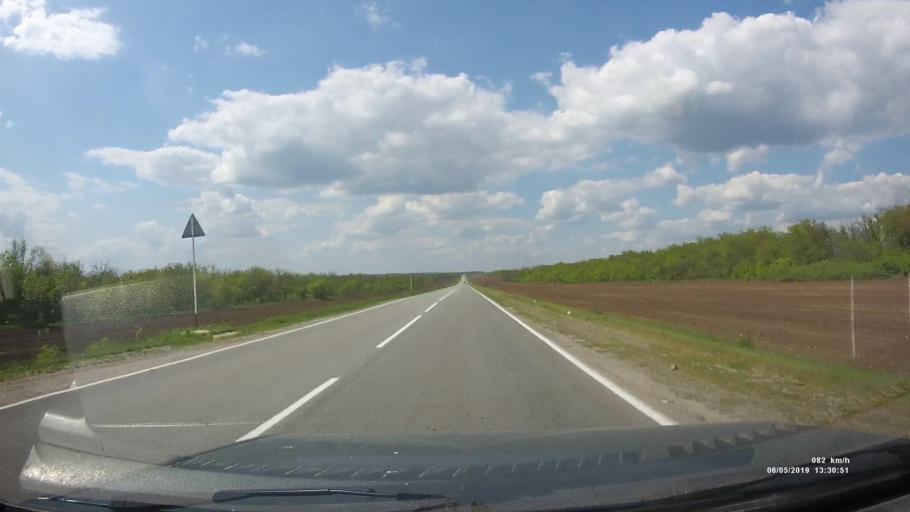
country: RU
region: Rostov
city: Ust'-Donetskiy
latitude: 47.6724
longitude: 40.8195
